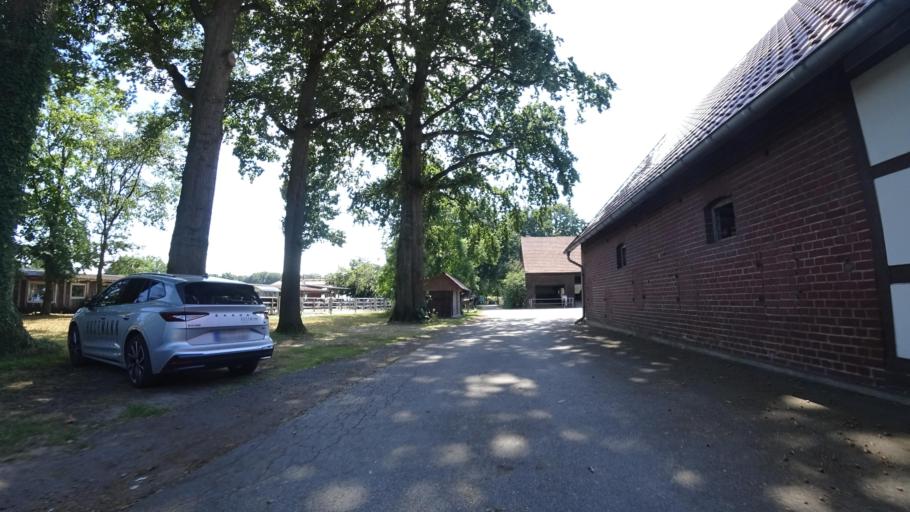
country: DE
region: North Rhine-Westphalia
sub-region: Regierungsbezirk Detmold
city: Guetersloh
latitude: 51.9451
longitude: 8.3933
